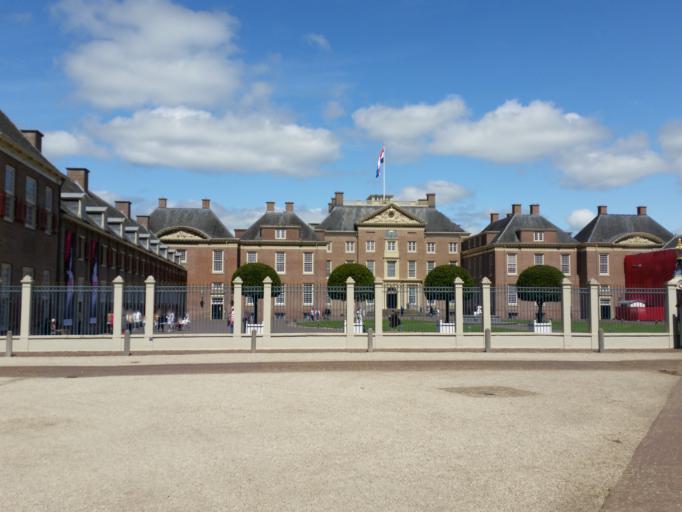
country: NL
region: Gelderland
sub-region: Gemeente Apeldoorn
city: Apeldoorn
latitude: 52.2330
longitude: 5.9457
